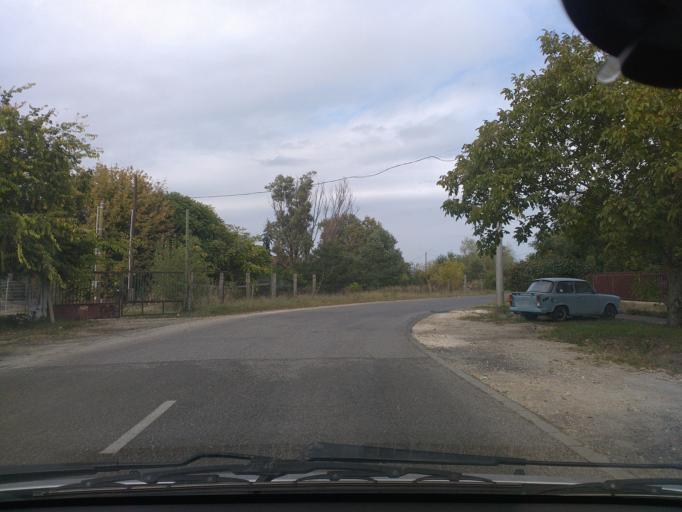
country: HU
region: Budapest
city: Budapest XVIII. keruelet
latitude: 47.4423
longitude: 19.2080
